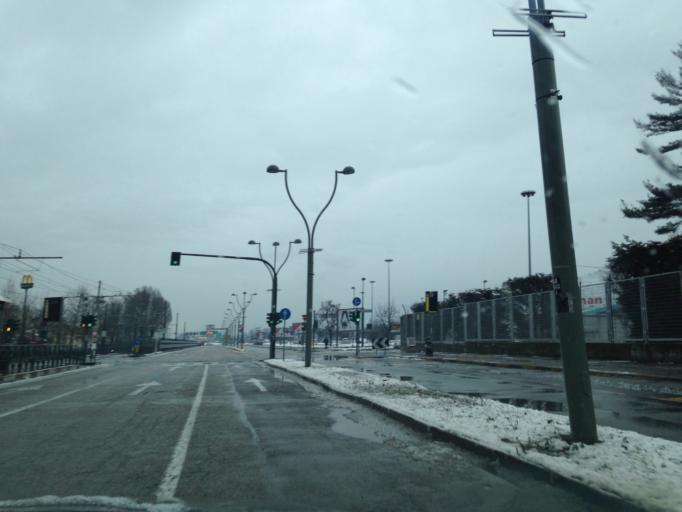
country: IT
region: Piedmont
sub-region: Provincia di Torino
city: Turin
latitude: 45.1156
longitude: 7.7091
